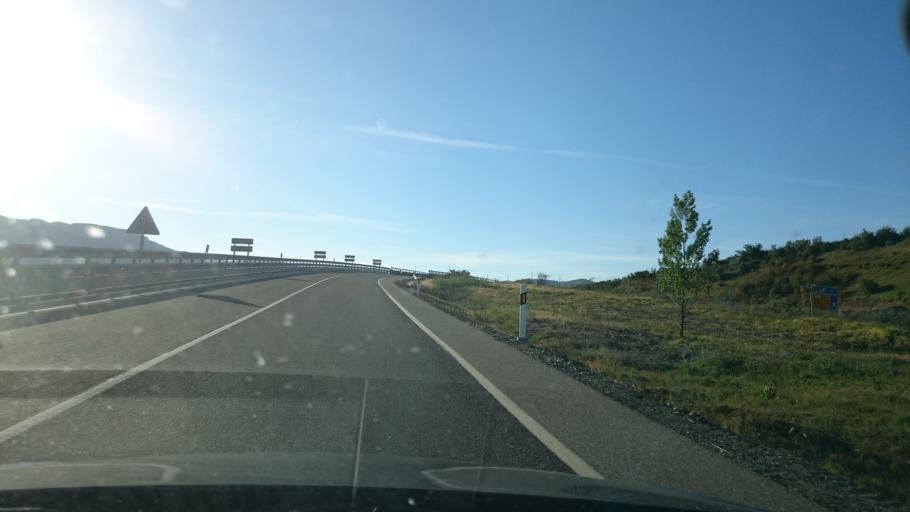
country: ES
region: Castille and Leon
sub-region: Provincia de Leon
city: Villadecanes
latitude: 42.5833
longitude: -6.7863
